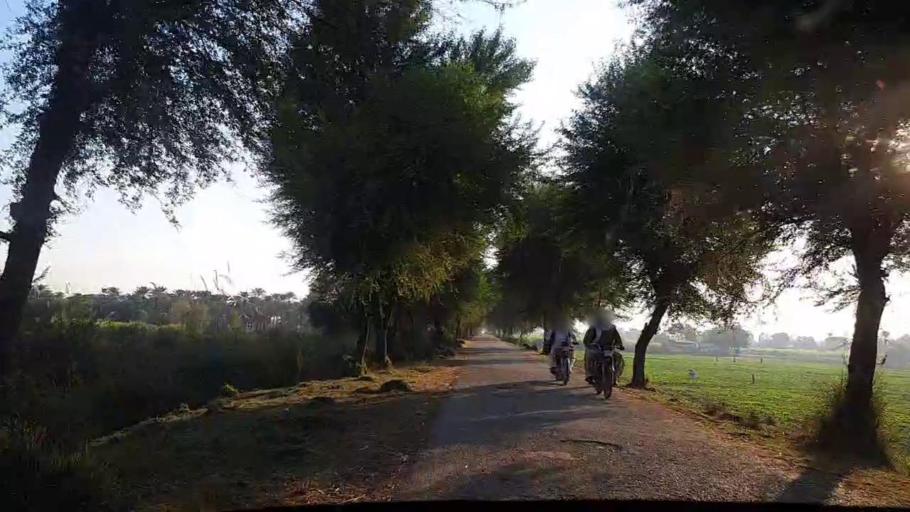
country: PK
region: Sindh
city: Sobhadero
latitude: 27.4052
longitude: 68.3917
